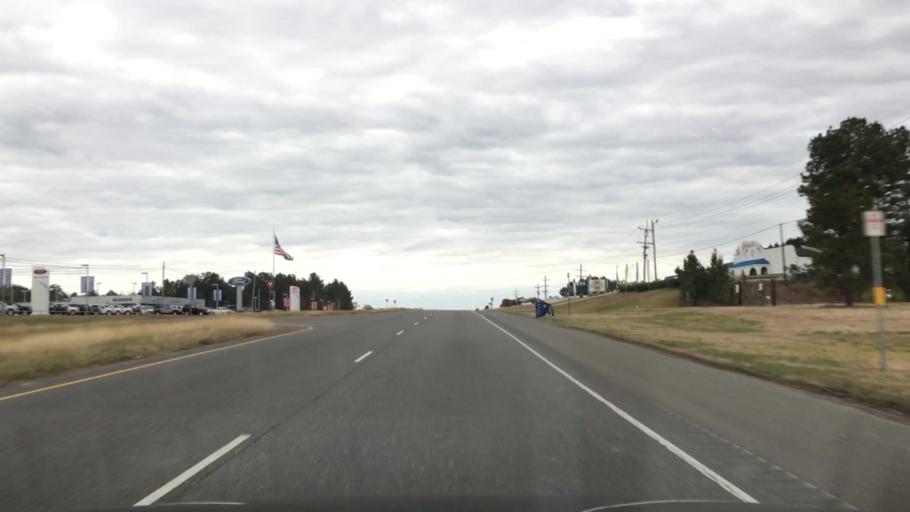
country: US
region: Louisiana
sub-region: Vernon Parish
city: New Llano
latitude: 31.0902
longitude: -93.2709
